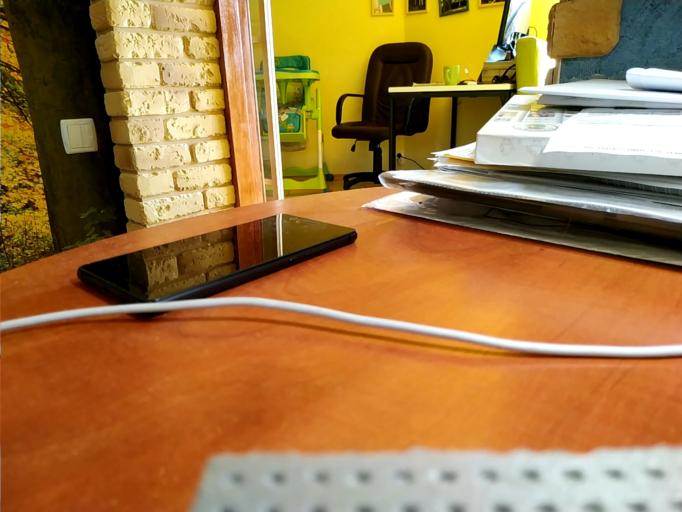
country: RU
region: Tverskaya
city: Kalashnikovo
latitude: 57.3734
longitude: 35.3964
